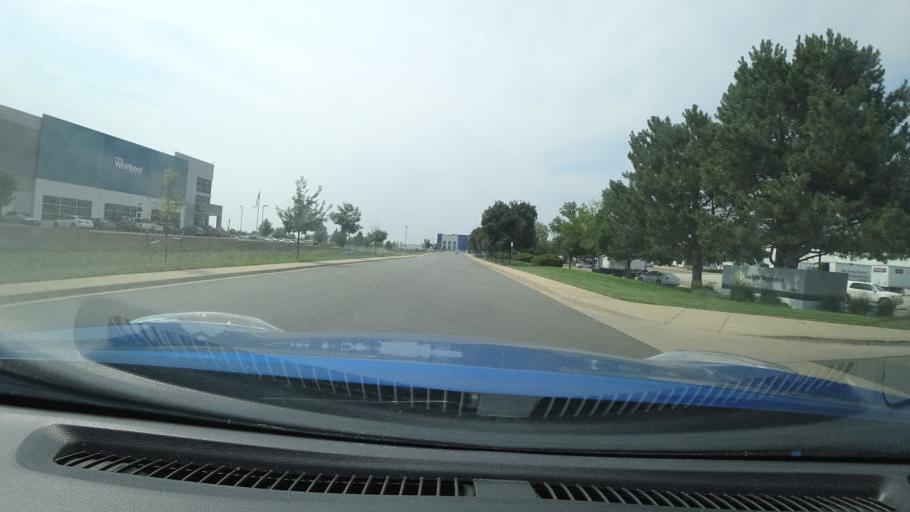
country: US
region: Colorado
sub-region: Adams County
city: Aurora
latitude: 39.7639
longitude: -104.7412
